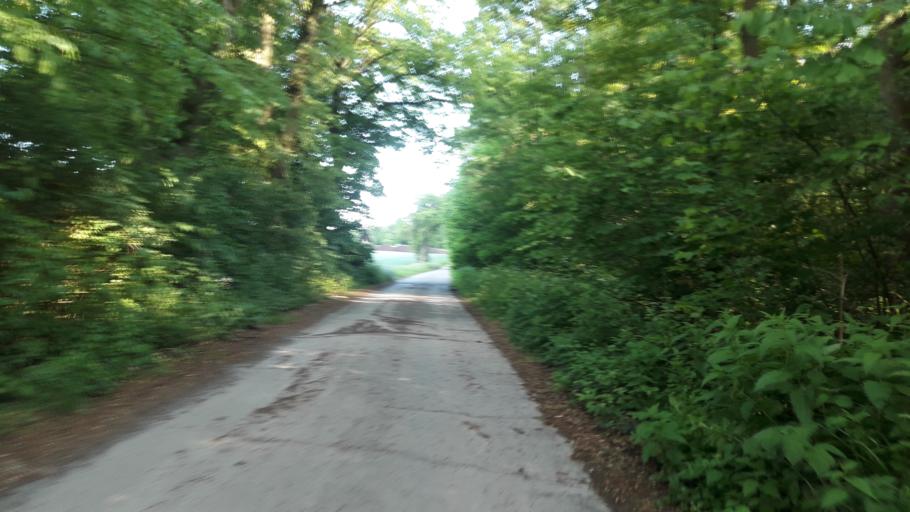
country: DE
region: North Rhine-Westphalia
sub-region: Regierungsbezirk Detmold
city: Paderborn
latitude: 51.6706
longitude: 8.7851
